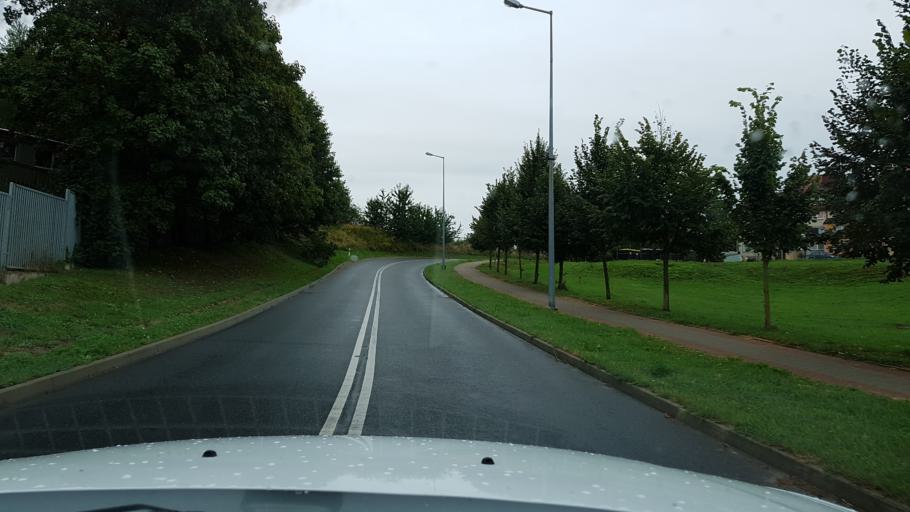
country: PL
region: West Pomeranian Voivodeship
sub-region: Powiat gryfinski
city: Cedynia
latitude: 52.8807
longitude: 14.2123
